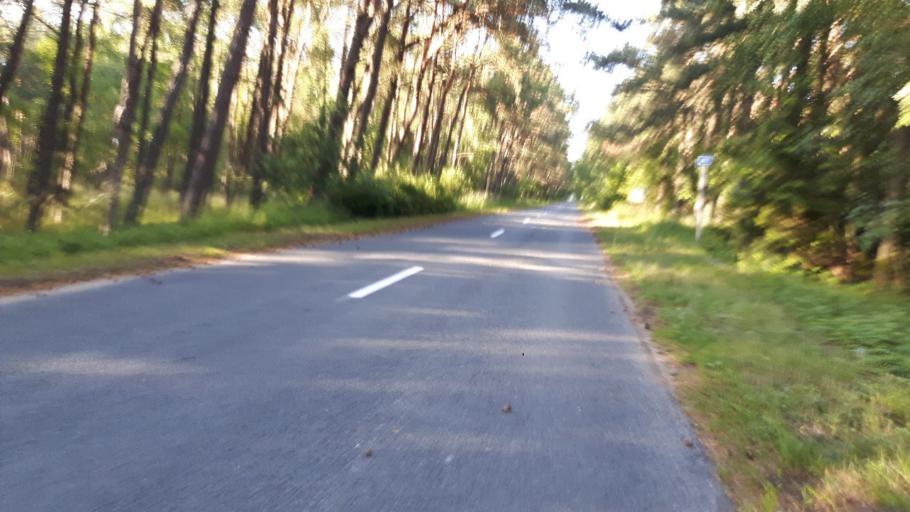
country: LT
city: Nida
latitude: 55.2568
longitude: 20.9345
